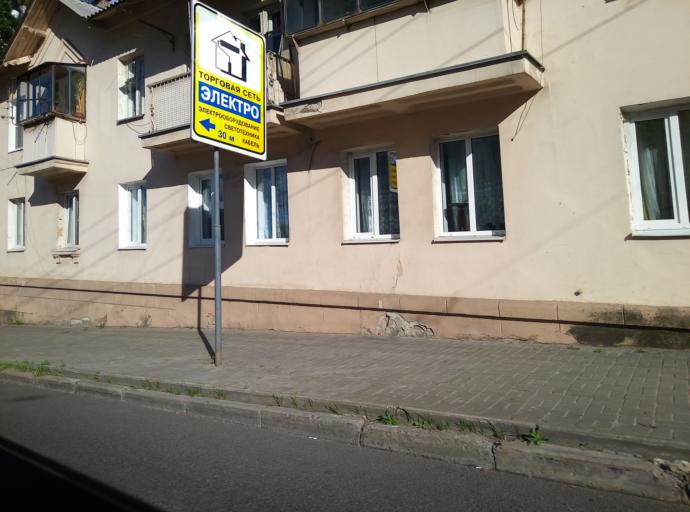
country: RU
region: Kursk
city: Kursk
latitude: 51.7237
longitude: 36.1835
